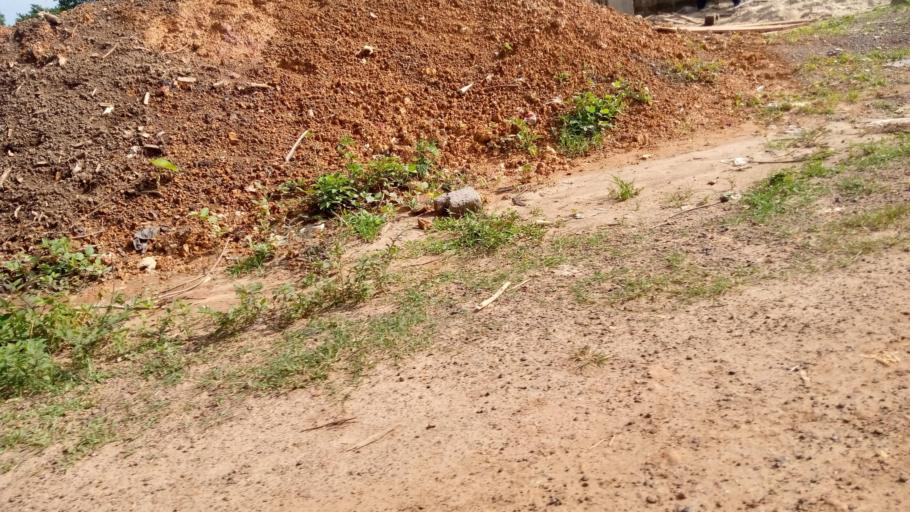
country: SL
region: Southern Province
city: Pujehun
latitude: 7.3537
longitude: -11.7215
